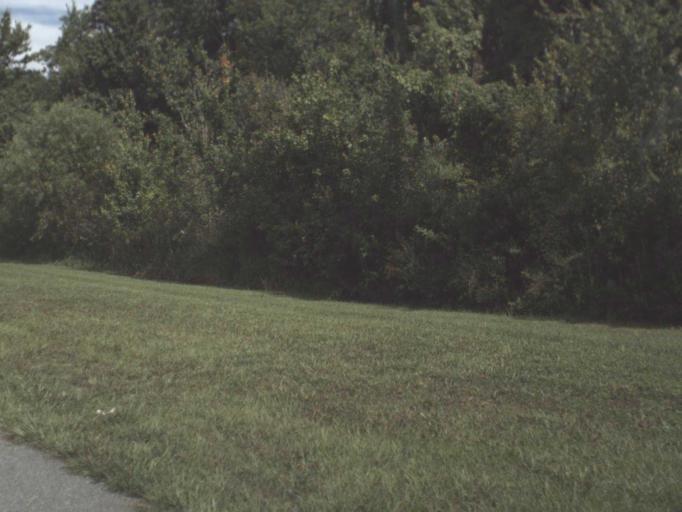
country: US
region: Florida
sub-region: Pasco County
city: Odessa
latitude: 28.1903
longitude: -82.5798
